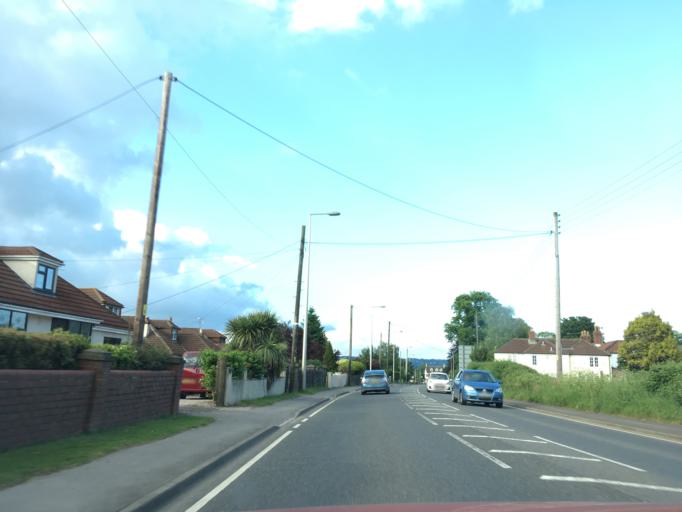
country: GB
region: England
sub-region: North Somerset
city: Churchill
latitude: 51.3360
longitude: -2.7917
